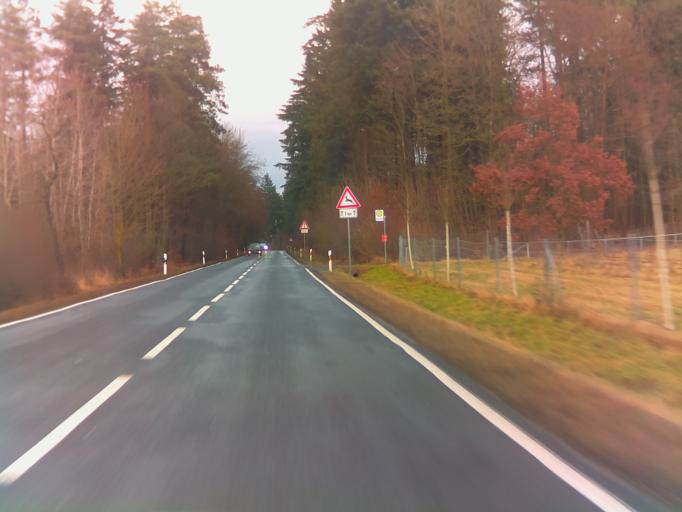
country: DE
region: Thuringia
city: Ellingshausen
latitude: 50.5724
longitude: 10.4544
